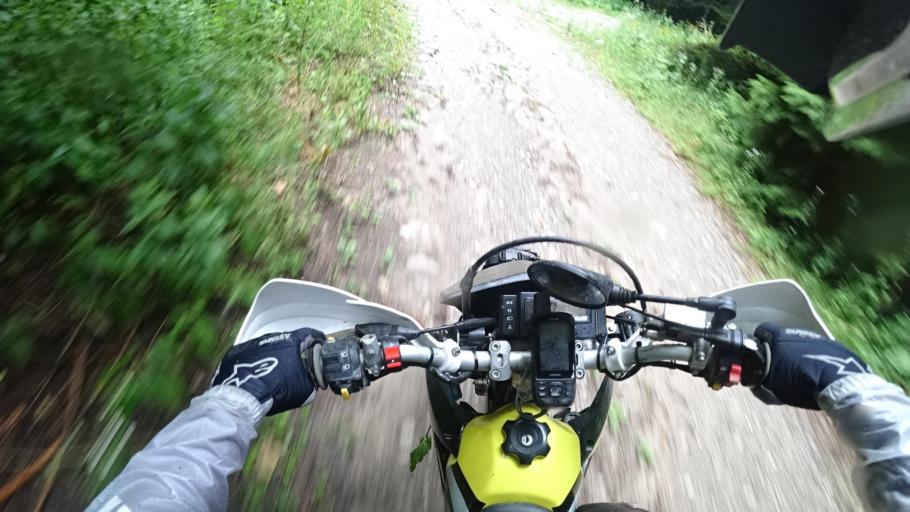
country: HR
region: Karlovacka
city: Plaski
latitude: 44.9360
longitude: 15.4100
